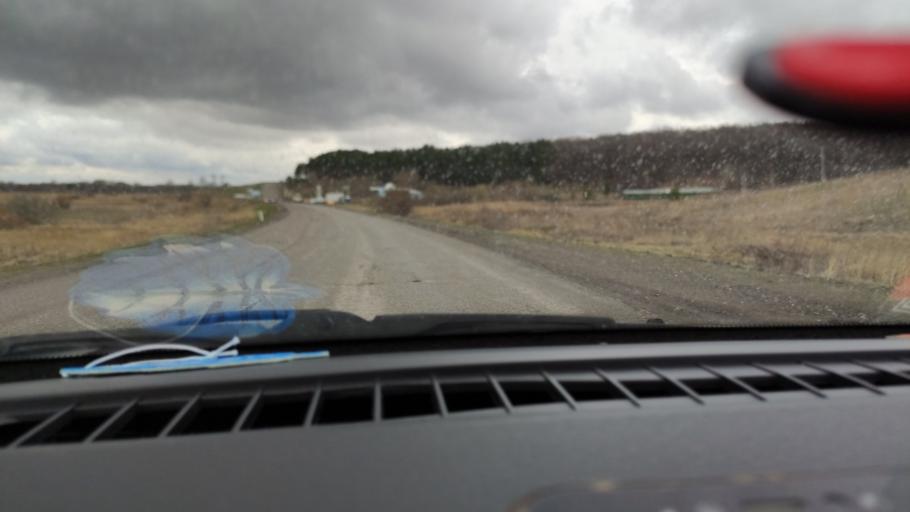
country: RU
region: Tatarstan
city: Nurlat
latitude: 54.3867
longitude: 50.7478
